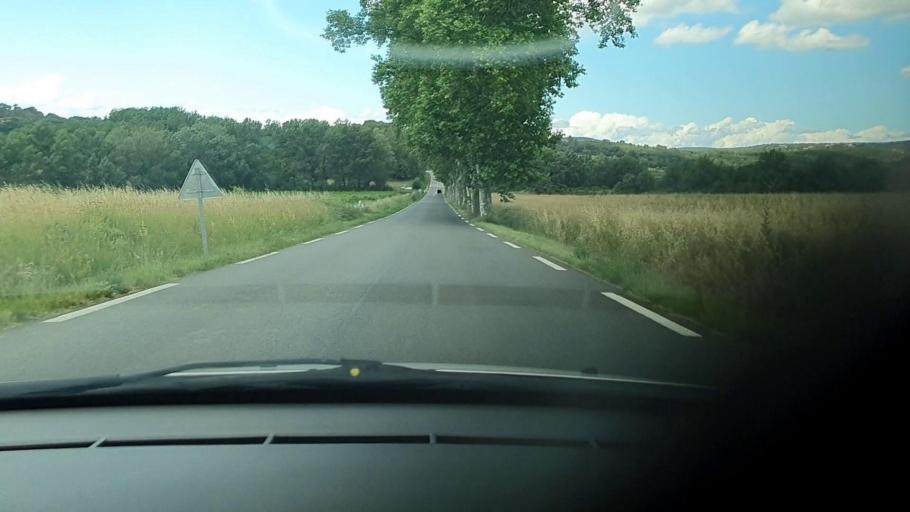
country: FR
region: Languedoc-Roussillon
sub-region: Departement du Gard
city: Montaren-et-Saint-Mediers
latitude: 44.0401
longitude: 4.3136
